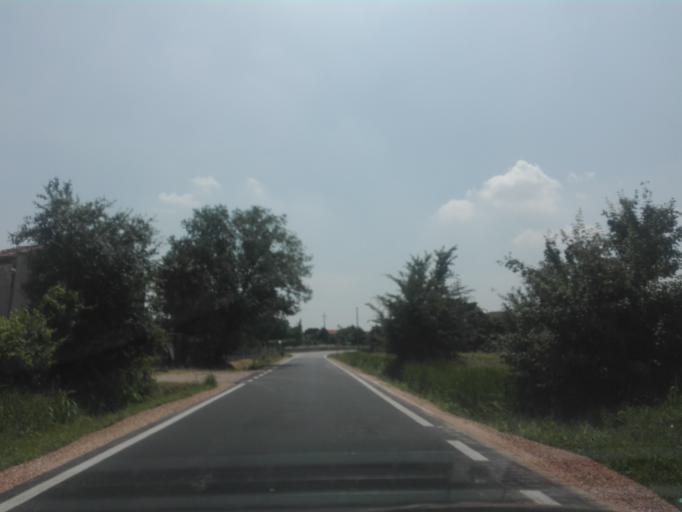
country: IT
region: Veneto
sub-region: Provincia di Rovigo
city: Grignano Polesine
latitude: 45.0500
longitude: 11.7494
